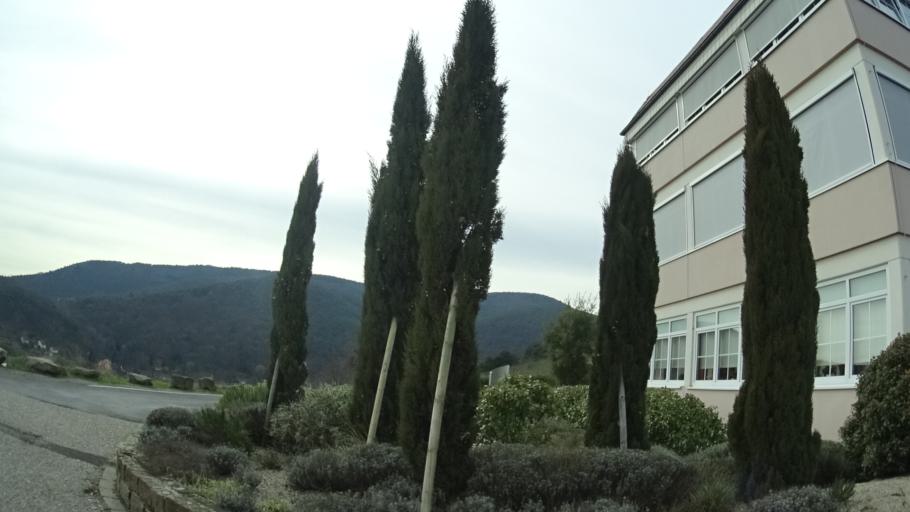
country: DE
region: Rheinland-Pfalz
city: Sankt Martin
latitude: 49.3029
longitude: 8.1004
